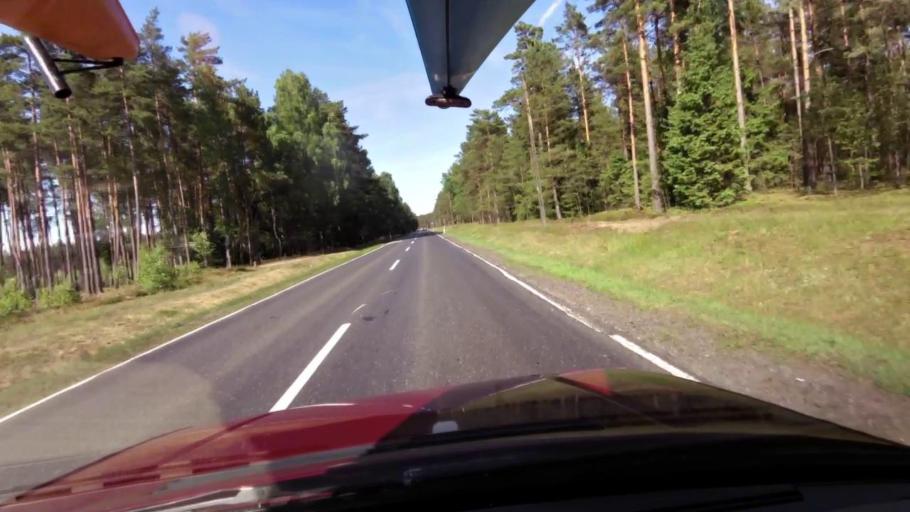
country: PL
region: Pomeranian Voivodeship
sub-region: Powiat bytowski
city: Trzebielino
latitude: 54.1611
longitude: 17.0530
